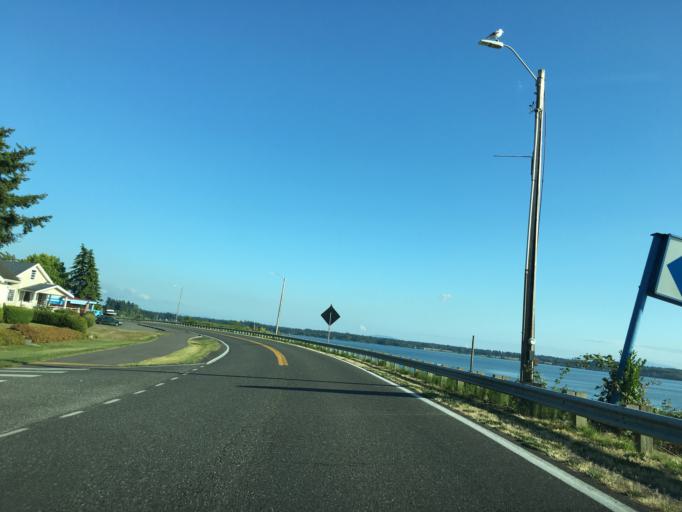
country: US
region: Washington
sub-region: Whatcom County
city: Blaine
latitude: 48.9887
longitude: -122.7516
